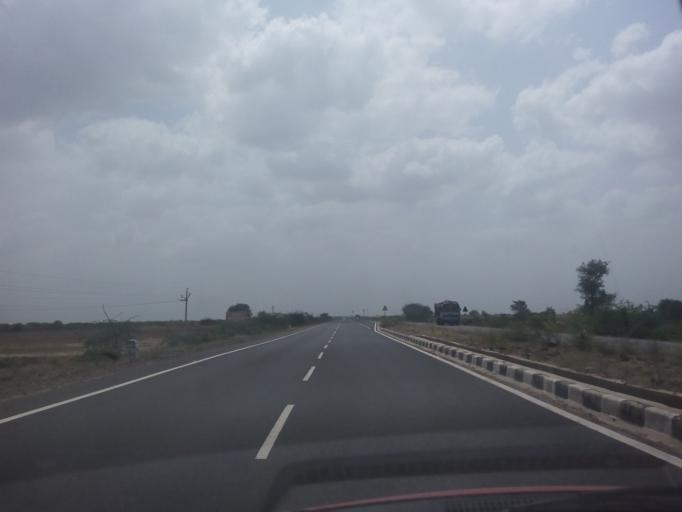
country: IN
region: Gujarat
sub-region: Surendranagar
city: Lakhtar
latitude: 23.0601
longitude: 71.7274
